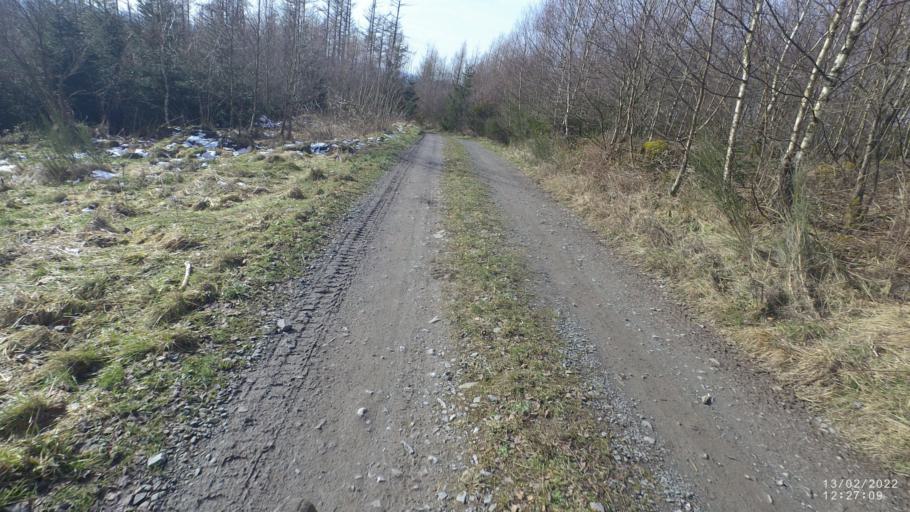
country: DE
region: North Rhine-Westphalia
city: Neuenrade
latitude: 51.2867
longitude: 7.7584
